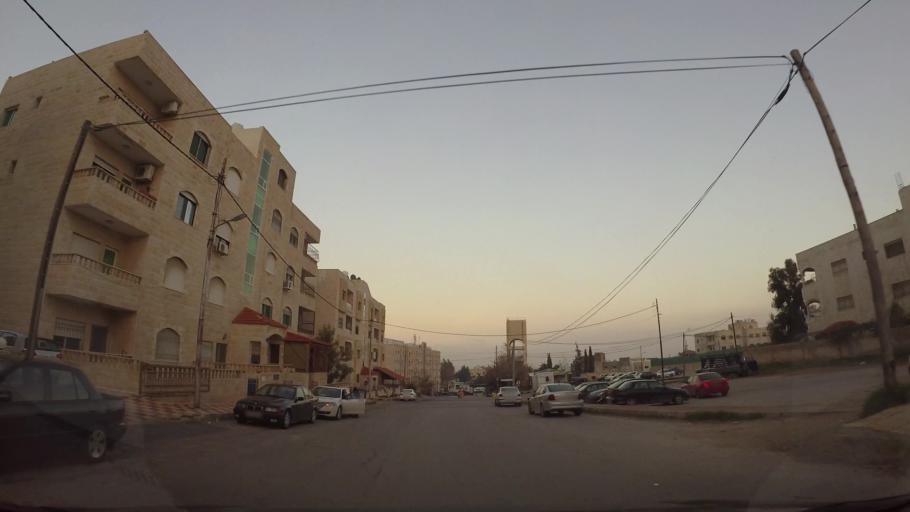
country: JO
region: Amman
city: Amman
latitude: 31.9927
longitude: 35.9612
